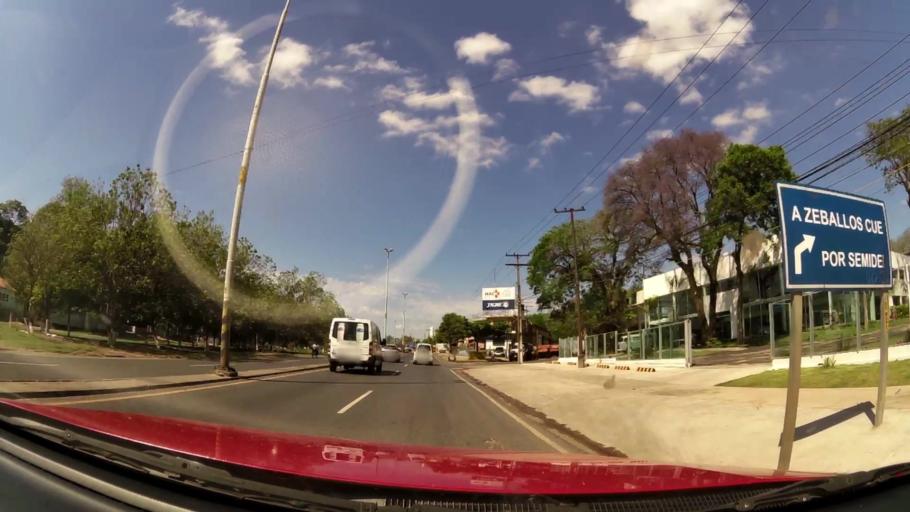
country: PY
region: Central
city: Colonia Mariano Roque Alonso
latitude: -25.2513
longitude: -57.5557
